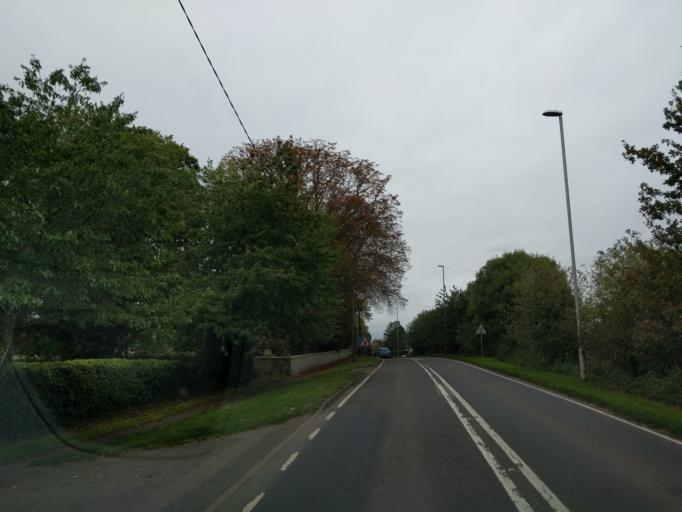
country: GB
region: England
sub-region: Cambridgeshire
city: Earith
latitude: 52.3511
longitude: 0.0151
